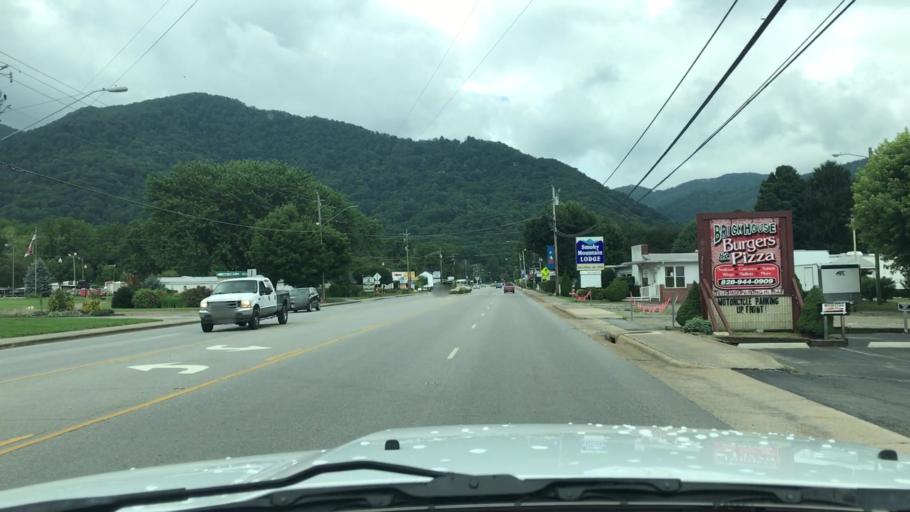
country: US
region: North Carolina
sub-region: Haywood County
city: Maggie Valley
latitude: 35.5178
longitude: -83.0935
